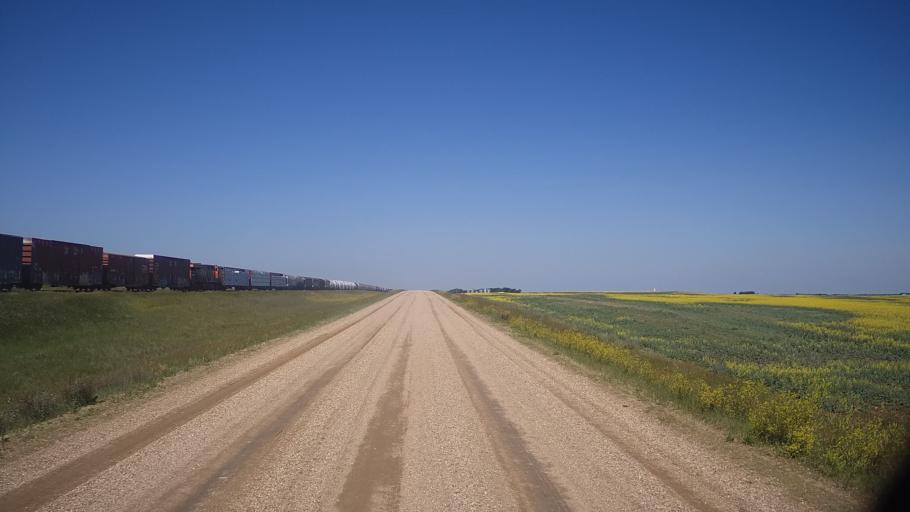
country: CA
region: Saskatchewan
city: Watrous
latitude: 51.8577
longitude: -105.9551
